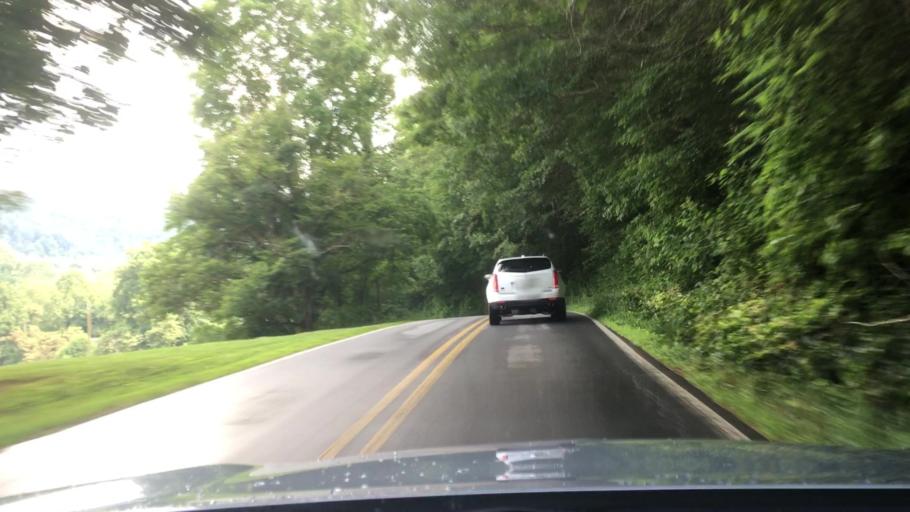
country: US
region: North Carolina
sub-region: Yancey County
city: Burnsville
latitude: 35.9065
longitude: -82.3591
